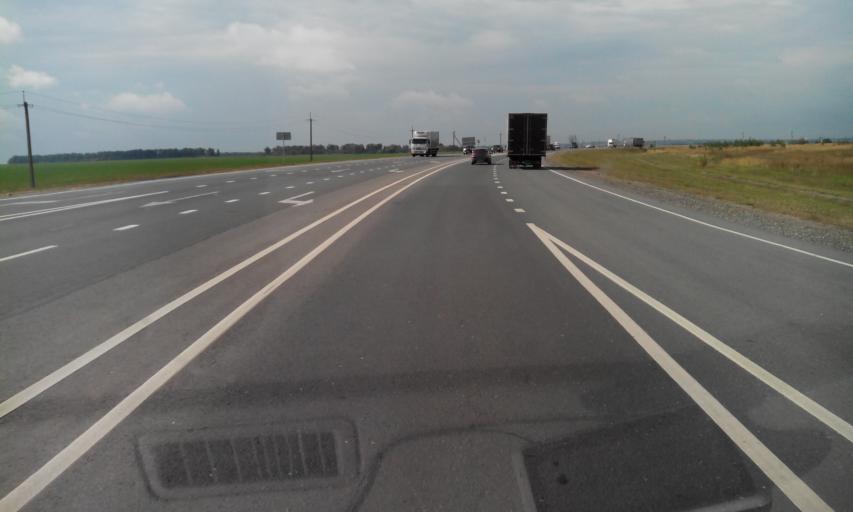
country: RU
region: Penza
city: Kuznetsk
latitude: 53.0827
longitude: 46.6053
